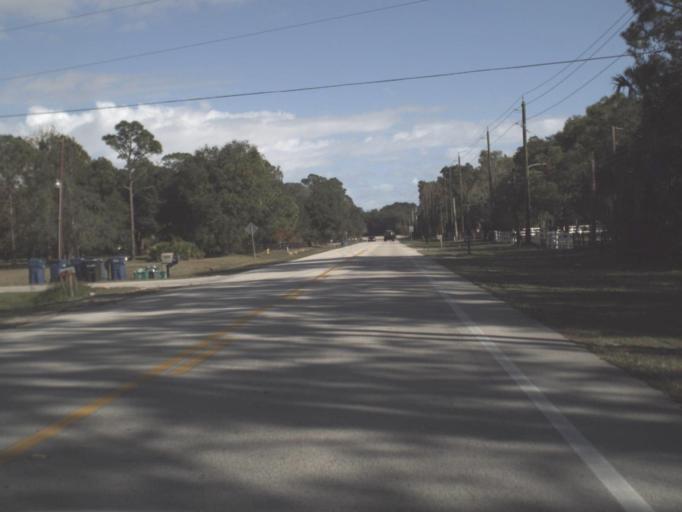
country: US
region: Florida
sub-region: Volusia County
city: Samsula-Spruce Creek
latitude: 29.0843
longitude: -81.0627
